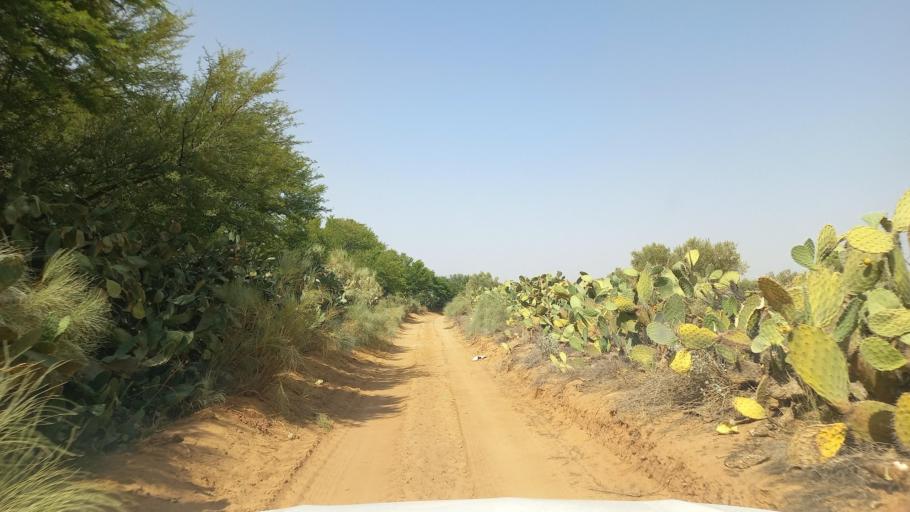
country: TN
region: Al Qasrayn
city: Kasserine
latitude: 35.2399
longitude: 9.0662
